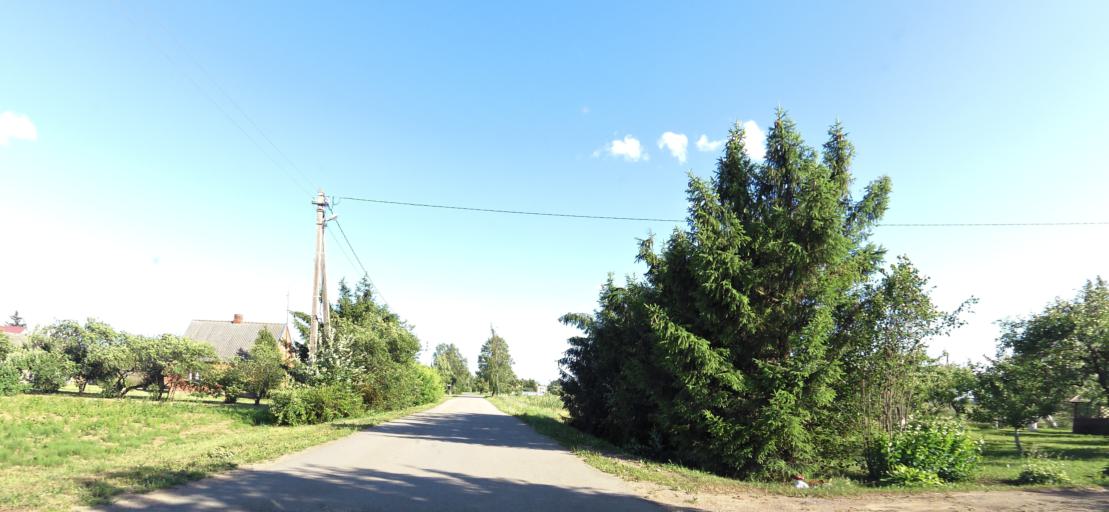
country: LT
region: Panevezys
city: Pasvalys
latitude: 56.1361
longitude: 24.5363
